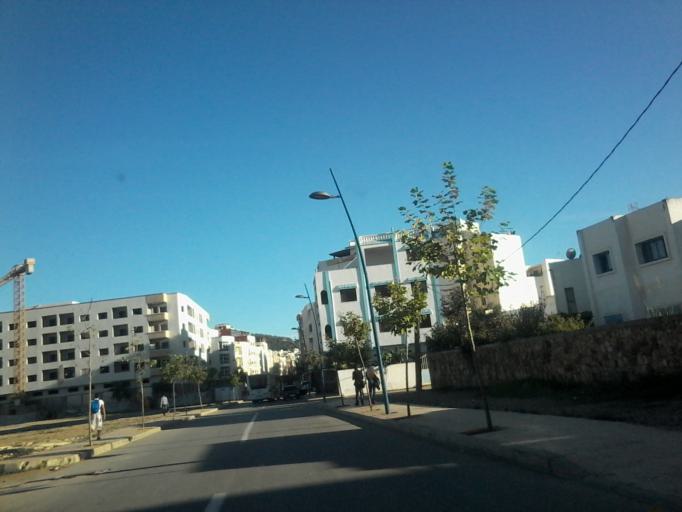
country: MA
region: Tanger-Tetouan
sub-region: Tetouan
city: Martil
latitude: 35.6887
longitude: -5.3281
